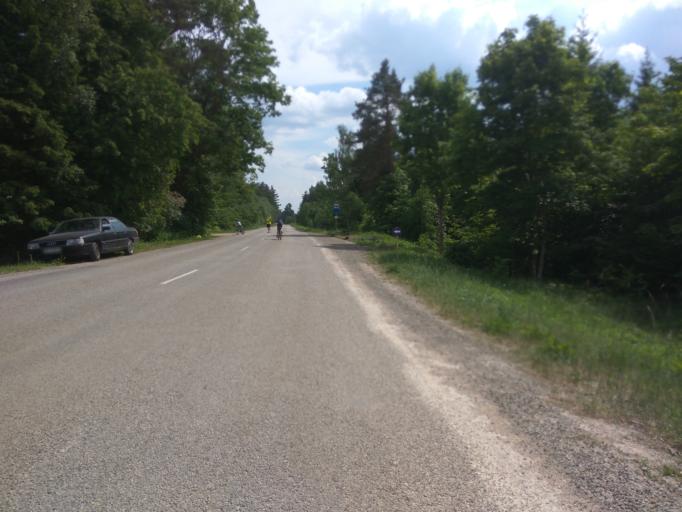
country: LV
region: Kuldigas Rajons
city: Kuldiga
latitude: 56.9042
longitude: 21.9381
